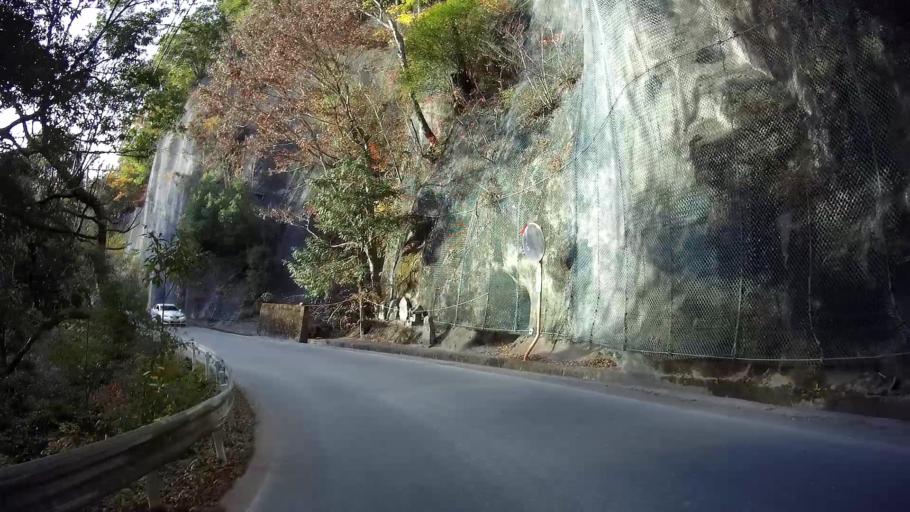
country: JP
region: Yamanashi
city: Fujikawaguchiko
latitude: 35.4751
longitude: 138.5401
